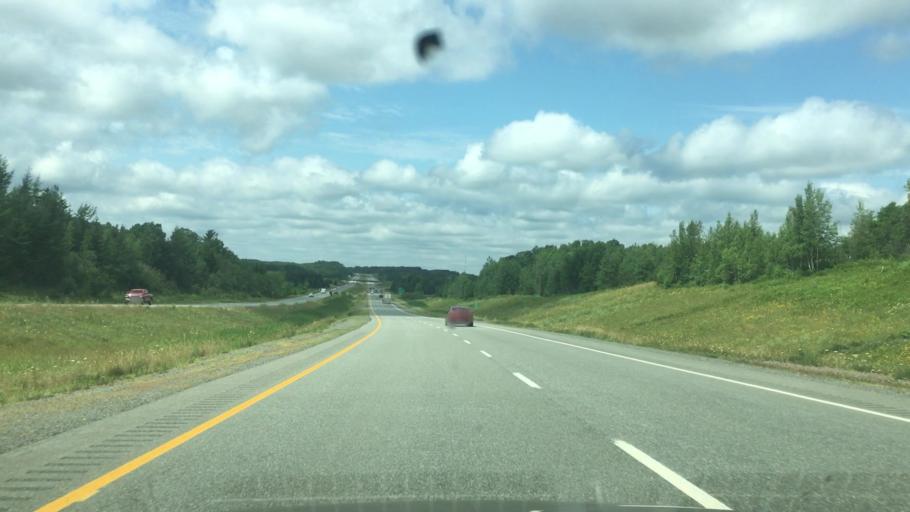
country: CA
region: Nova Scotia
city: Oxford
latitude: 45.7218
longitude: -63.8618
